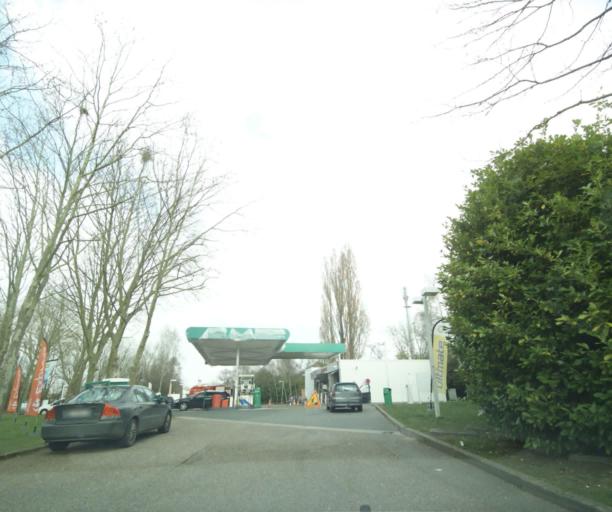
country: FR
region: Ile-de-France
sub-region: Departement du Val-d'Oise
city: Vaureal
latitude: 49.0463
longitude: 2.0246
